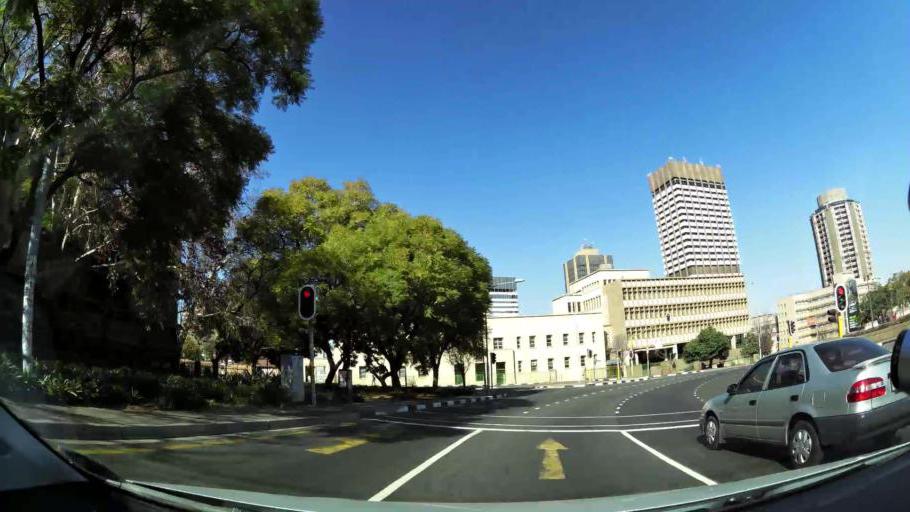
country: ZA
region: Gauteng
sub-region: City of Johannesburg Metropolitan Municipality
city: Johannesburg
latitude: -26.1922
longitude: 28.0414
